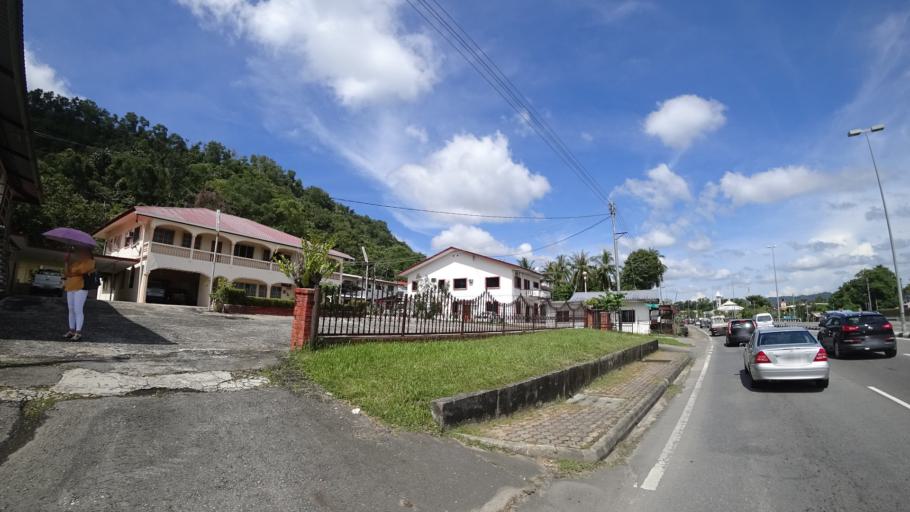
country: BN
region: Brunei and Muara
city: Bandar Seri Begawan
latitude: 4.8525
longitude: 114.8834
